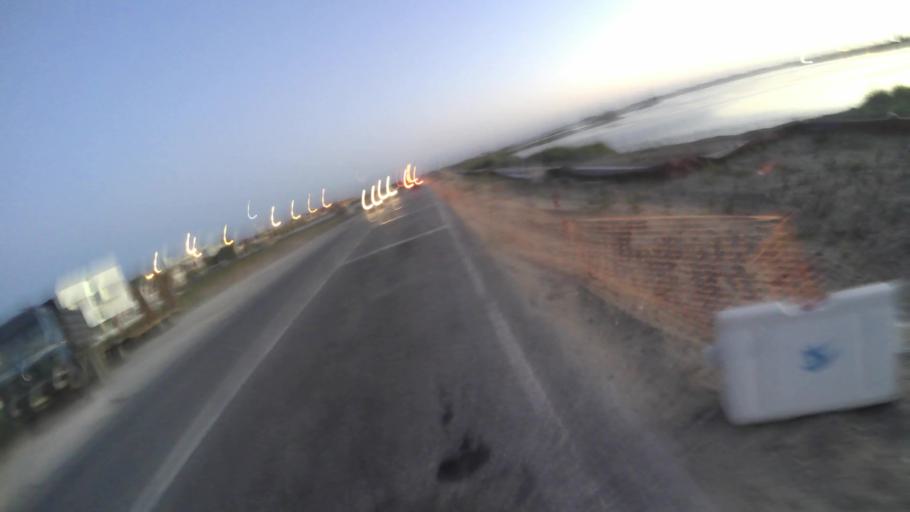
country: PT
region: Aveiro
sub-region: Aveiro
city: Aveiro
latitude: 40.6394
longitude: -8.6595
